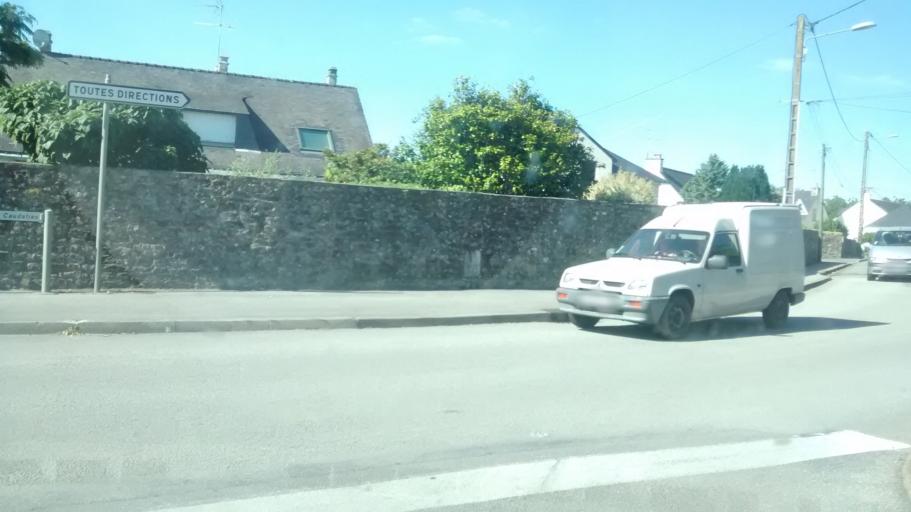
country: FR
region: Brittany
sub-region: Departement du Morbihan
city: Questembert
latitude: 47.6629
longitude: -2.4537
